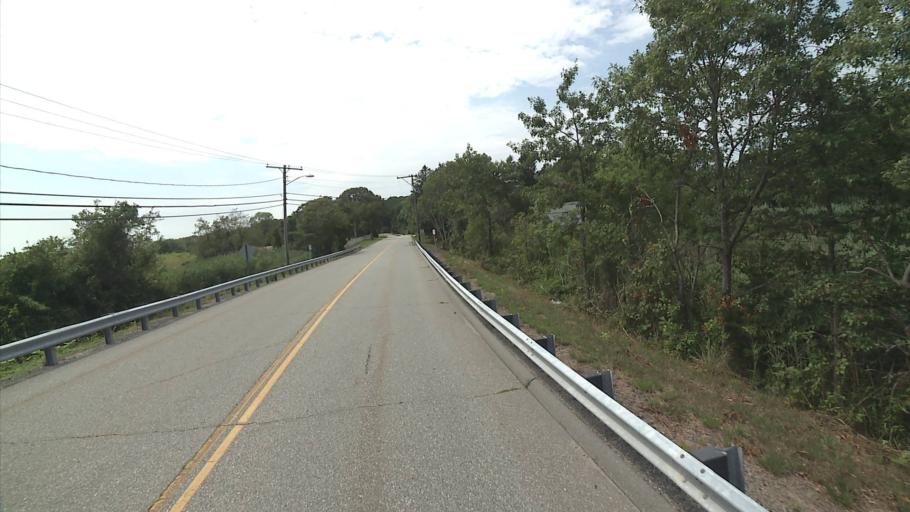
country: US
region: Connecticut
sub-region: New London County
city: Central Waterford
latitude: 41.3069
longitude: -72.1180
